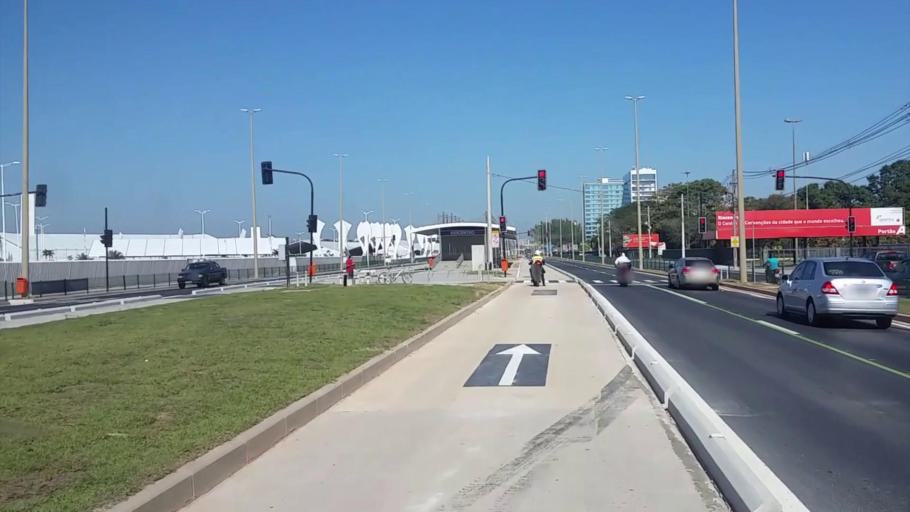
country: BR
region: Rio de Janeiro
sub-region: Nilopolis
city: Nilopolis
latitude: -22.9697
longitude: -43.3998
